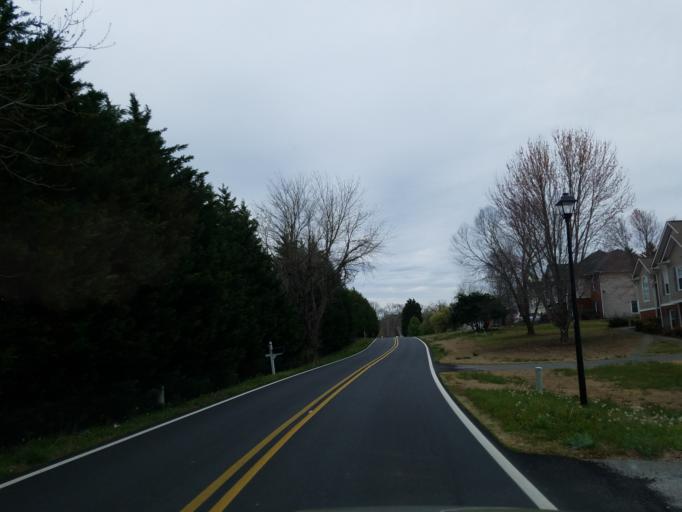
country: US
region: Georgia
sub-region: Bartow County
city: Cartersville
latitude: 34.2151
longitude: -84.7795
